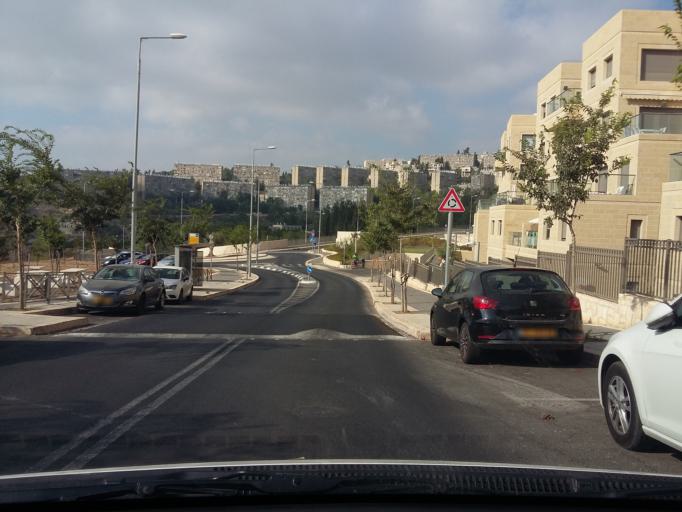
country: PS
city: Khallat Hamamah
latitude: 31.7623
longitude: 35.1690
